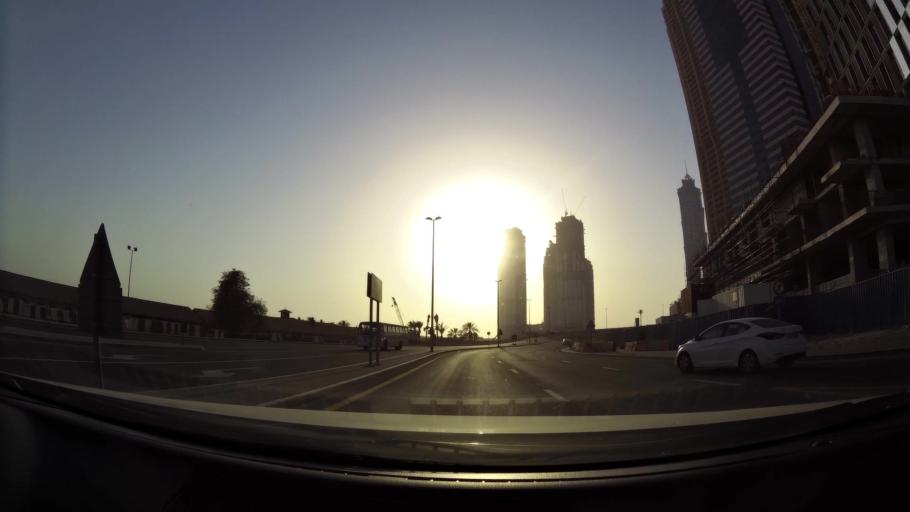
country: AE
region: Dubai
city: Dubai
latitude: 25.1793
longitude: 55.2638
